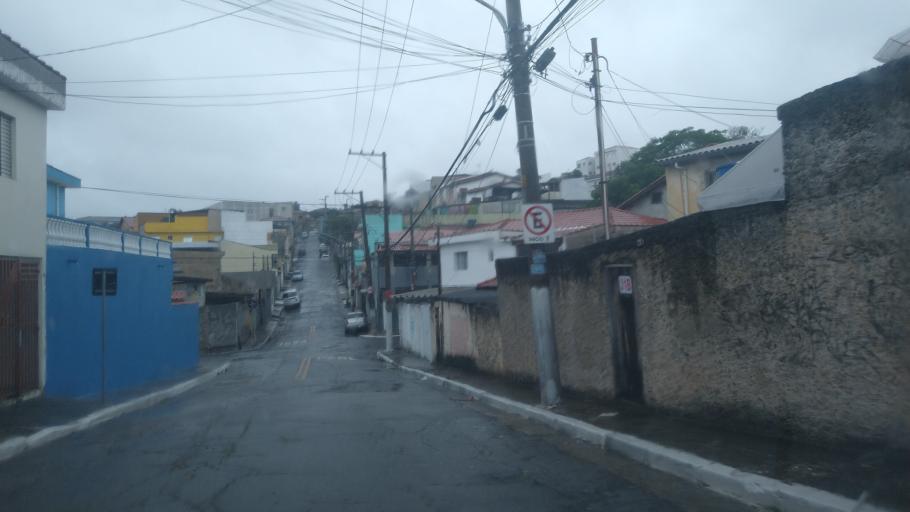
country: BR
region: Sao Paulo
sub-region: Sao Paulo
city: Sao Paulo
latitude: -23.4965
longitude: -46.5956
